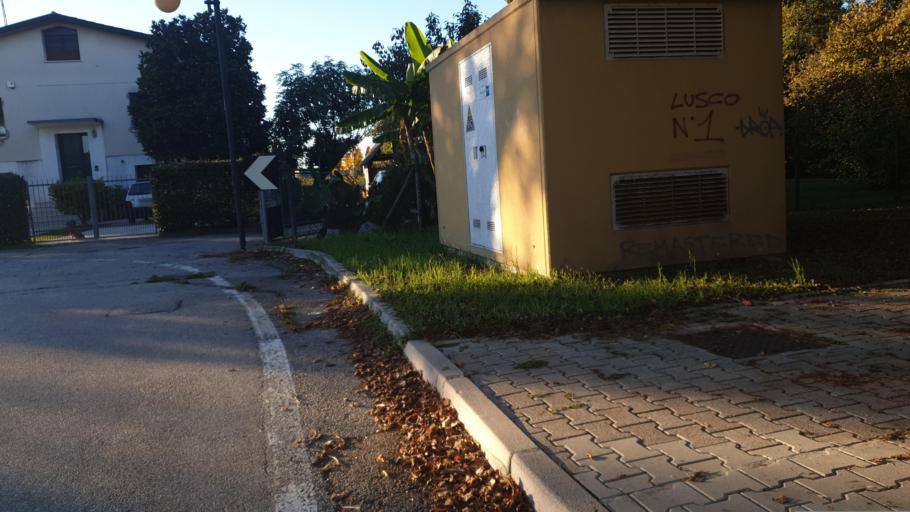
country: IT
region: Veneto
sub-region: Provincia di Venezia
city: Marano
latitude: 45.4549
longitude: 12.1012
